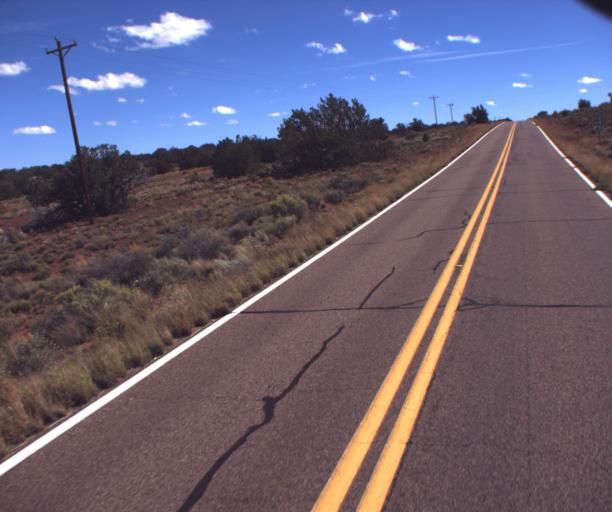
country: US
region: Arizona
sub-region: Apache County
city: Saint Johns
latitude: 34.5954
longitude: -109.6491
